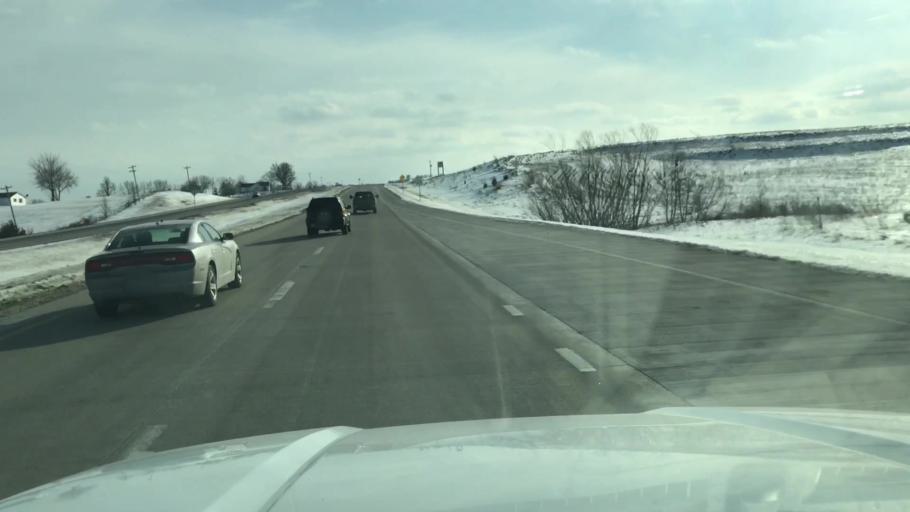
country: US
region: Missouri
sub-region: Nodaway County
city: Maryville
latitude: 40.3050
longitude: -94.8748
